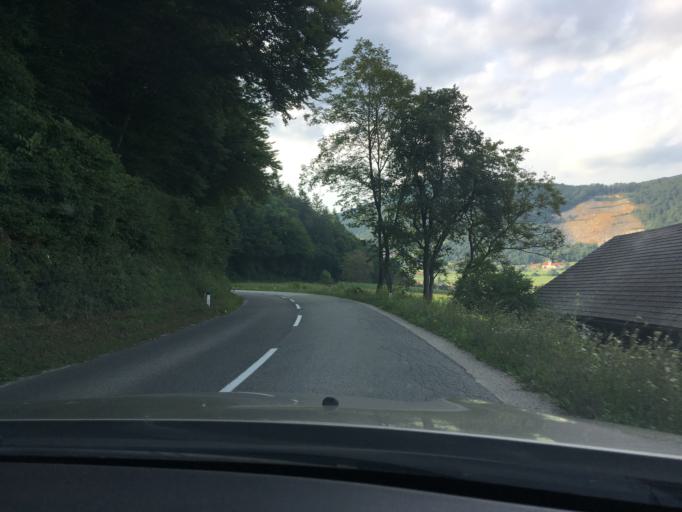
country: SI
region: Dolenjske Toplice
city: Dolenjske Toplice
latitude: 45.7703
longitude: 15.0238
